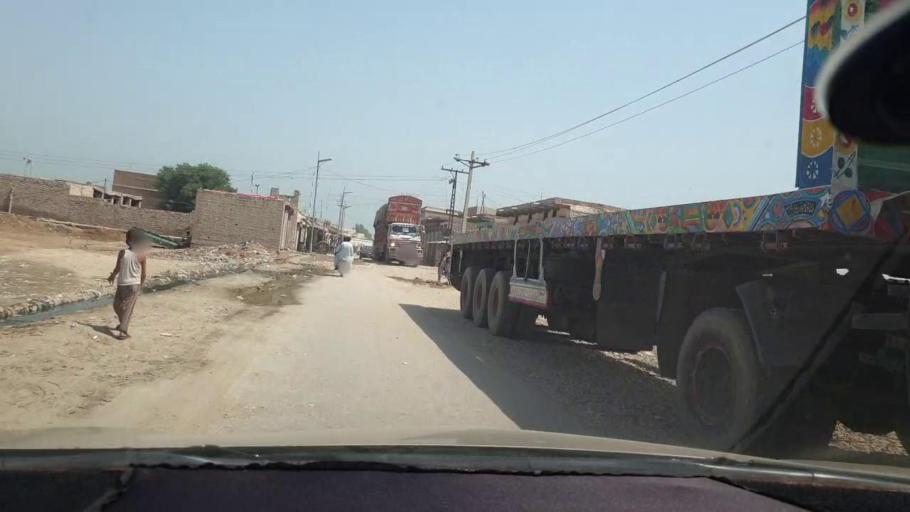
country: PK
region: Sindh
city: Kambar
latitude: 27.5973
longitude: 67.9977
